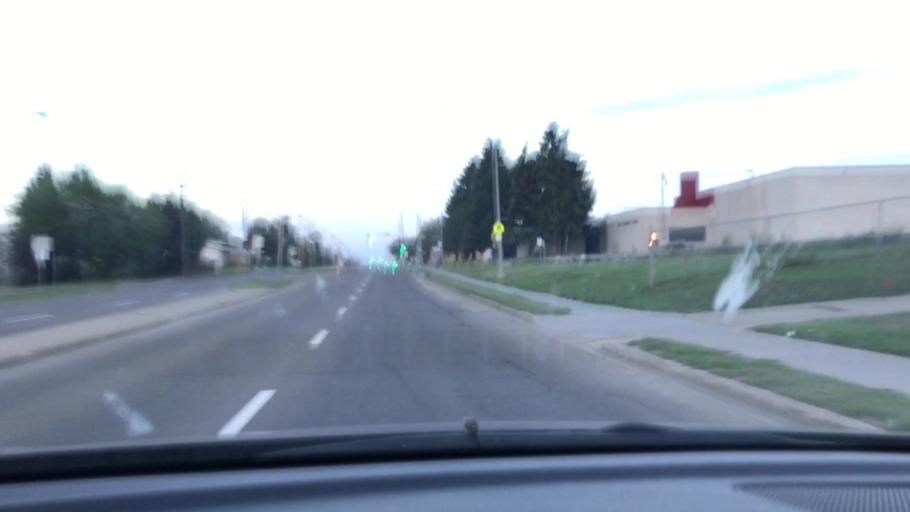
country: CA
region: Alberta
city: Edmonton
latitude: 53.4882
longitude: -113.5106
